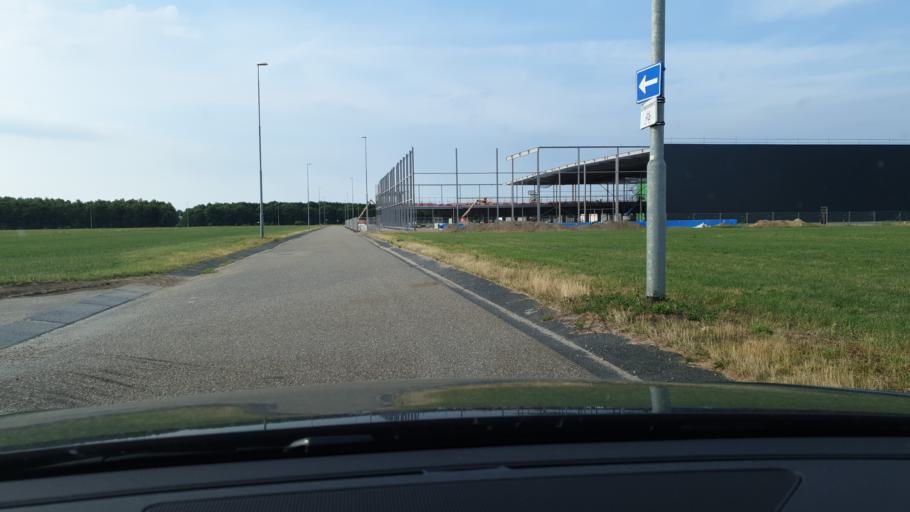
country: NL
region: North Brabant
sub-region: Gemeente Veldhoven
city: Oerle
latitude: 51.4396
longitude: 5.3835
